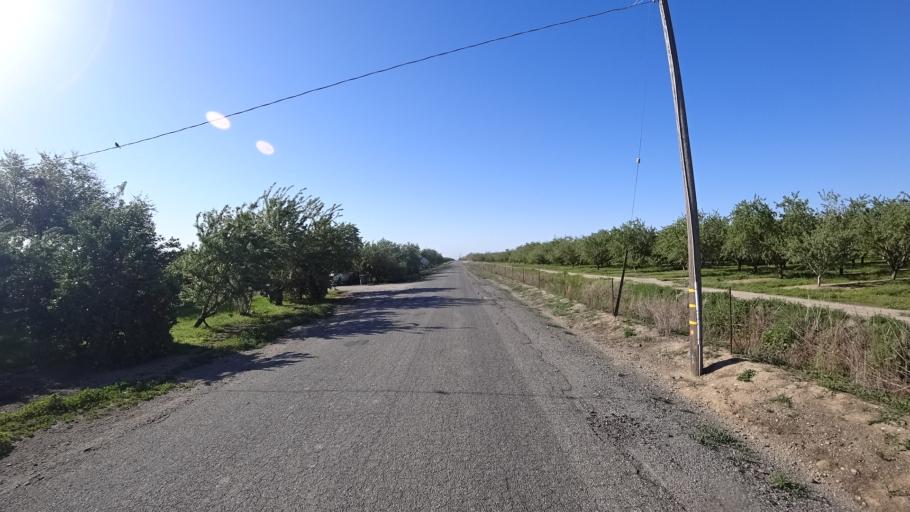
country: US
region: California
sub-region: Glenn County
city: Hamilton City
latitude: 39.7077
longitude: -122.0644
